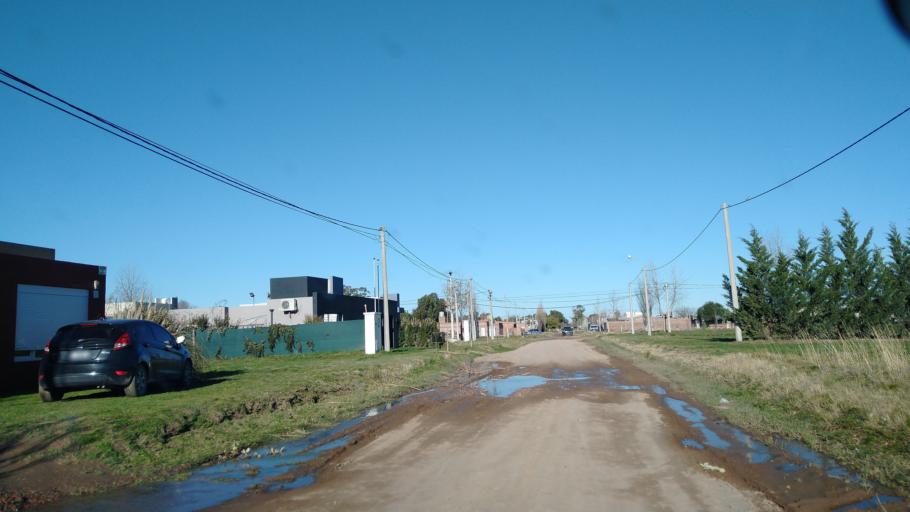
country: AR
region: Buenos Aires
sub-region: Partido de Bahia Blanca
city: Bahia Blanca
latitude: -38.7107
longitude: -62.2006
